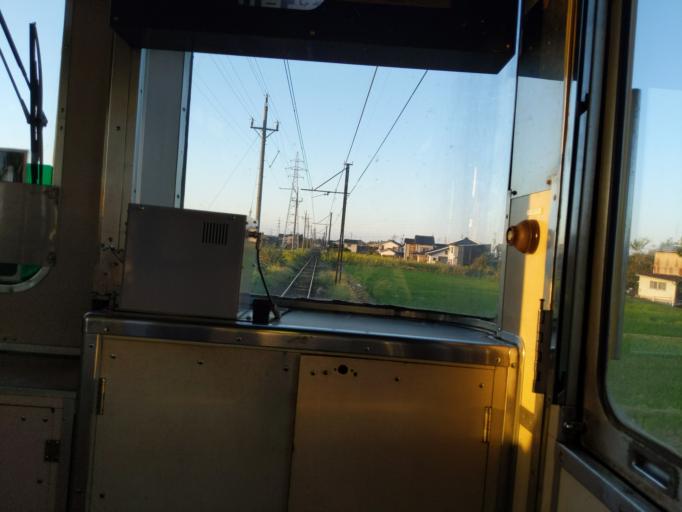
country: JP
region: Toyama
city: Kamiichi
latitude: 36.6846
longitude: 137.3177
